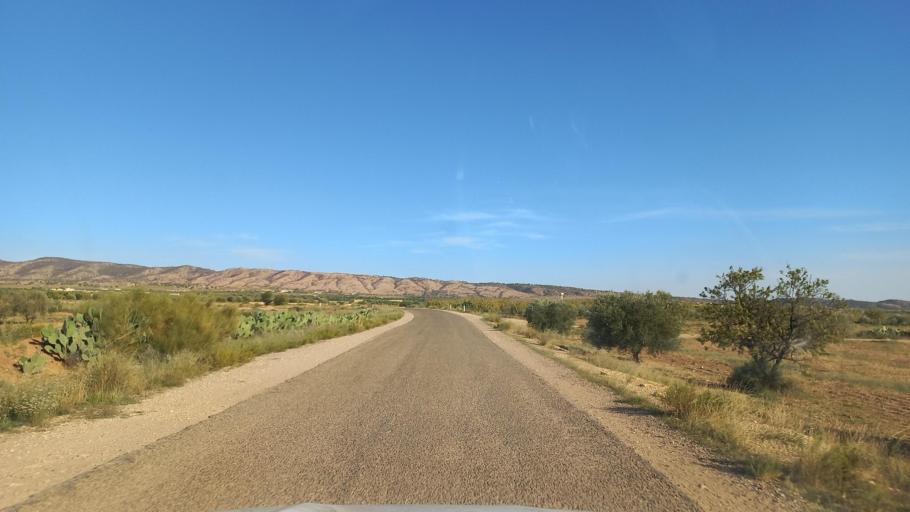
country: TN
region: Al Qasrayn
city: Sbiba
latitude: 35.3346
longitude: 9.1009
